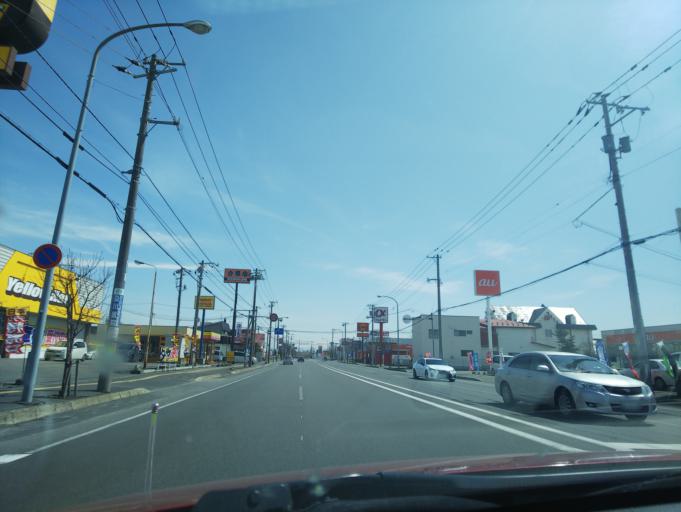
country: JP
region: Hokkaido
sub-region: Asahikawa-shi
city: Asahikawa
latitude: 43.7842
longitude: 142.4125
